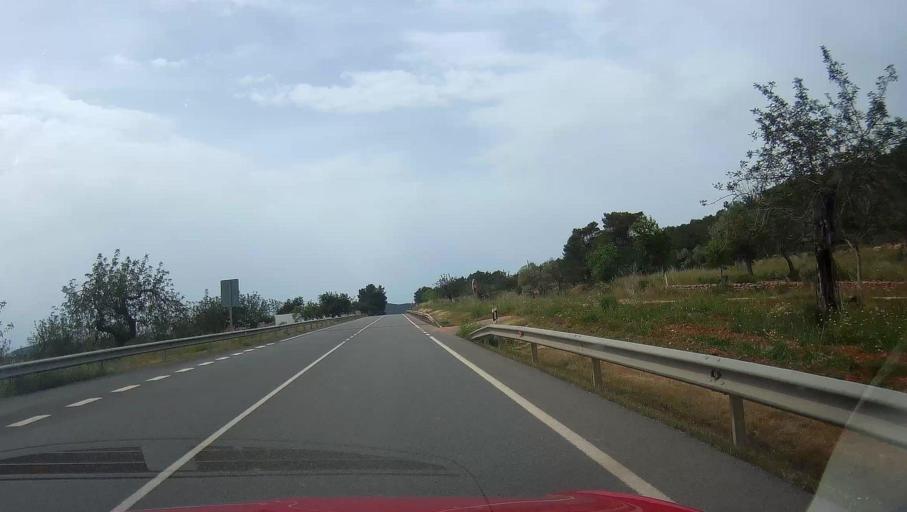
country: ES
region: Balearic Islands
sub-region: Illes Balears
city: Sant Joan de Labritja
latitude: 39.0383
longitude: 1.4918
